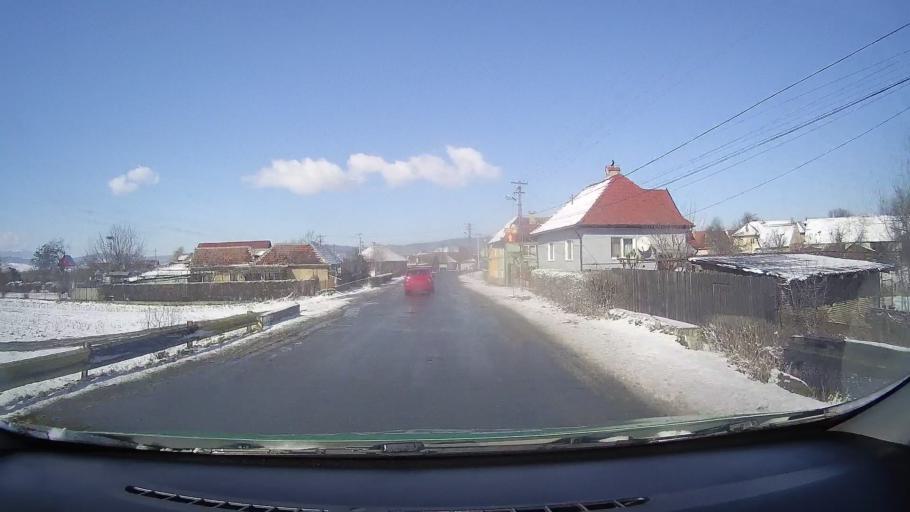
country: RO
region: Sibiu
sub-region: Comuna Avrig
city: Avrig
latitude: 45.7203
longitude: 24.3733
